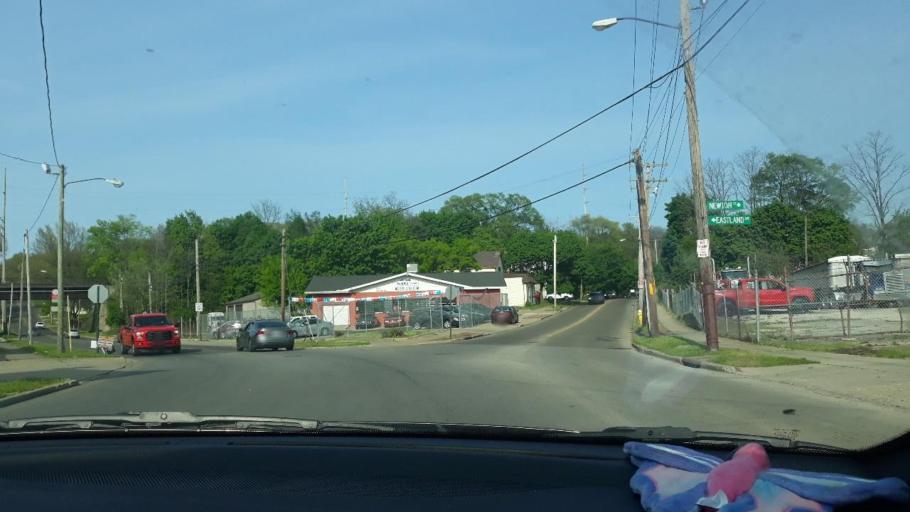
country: US
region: Ohio
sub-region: Summit County
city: Akron
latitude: 41.0732
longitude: -81.4832
